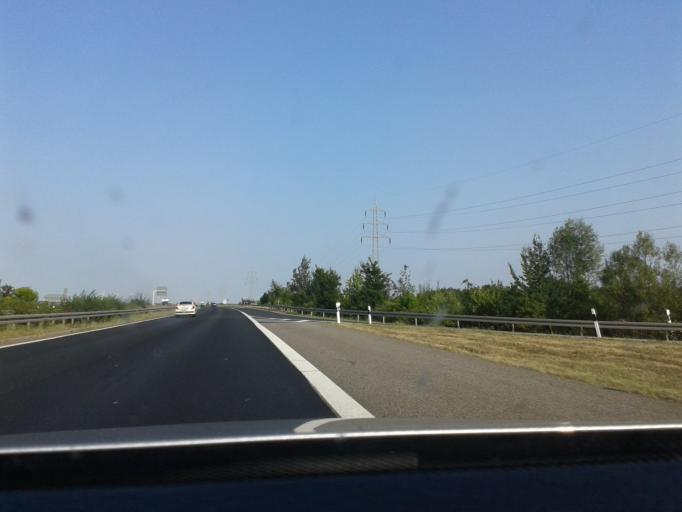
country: DE
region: Saxony-Anhalt
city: Edersleben
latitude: 51.4484
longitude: 11.2623
